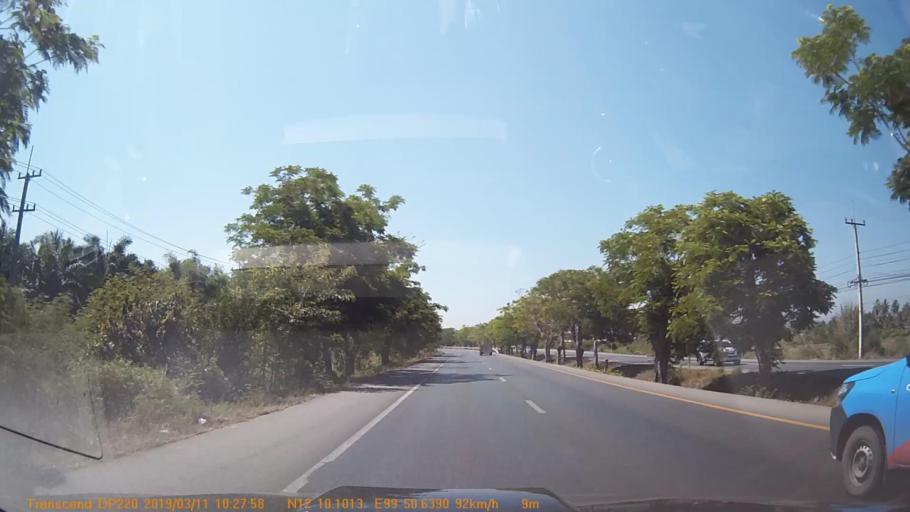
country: TH
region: Prachuap Khiri Khan
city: Kui Buri
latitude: 12.1680
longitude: 99.8440
